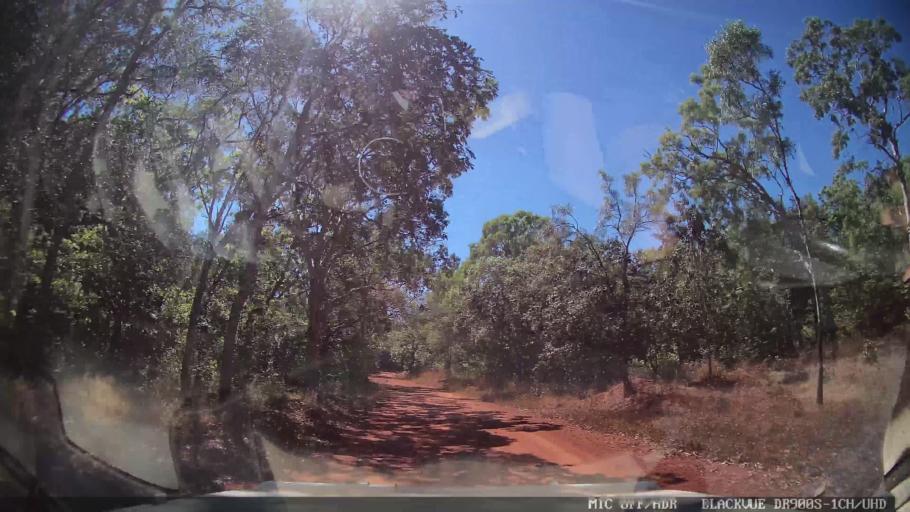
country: AU
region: Queensland
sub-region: Torres
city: Thursday Island
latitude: -10.7795
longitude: 142.4879
